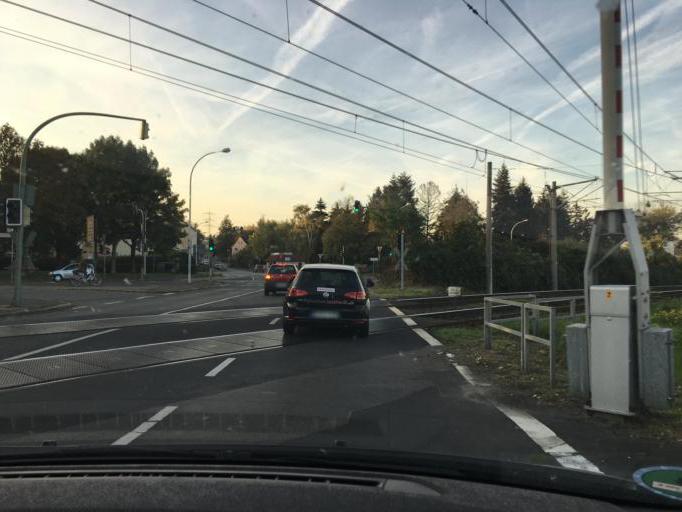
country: DE
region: North Rhine-Westphalia
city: Bruhl
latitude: 50.8413
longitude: 6.9002
